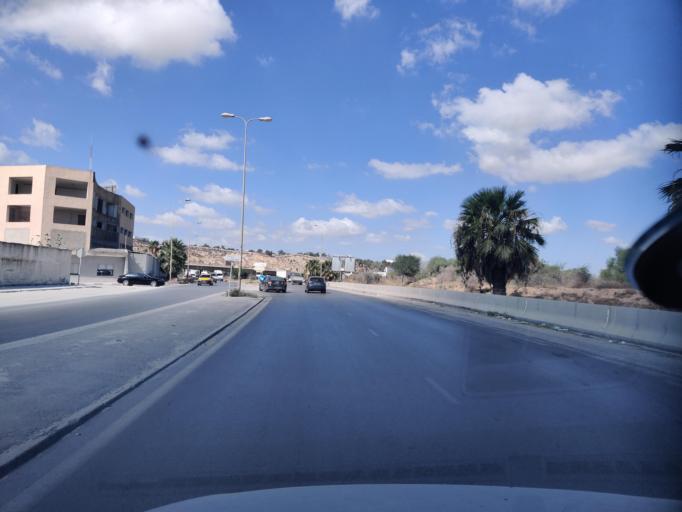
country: TN
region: Bin 'Arus
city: Ben Arous
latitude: 36.7810
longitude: 10.2011
